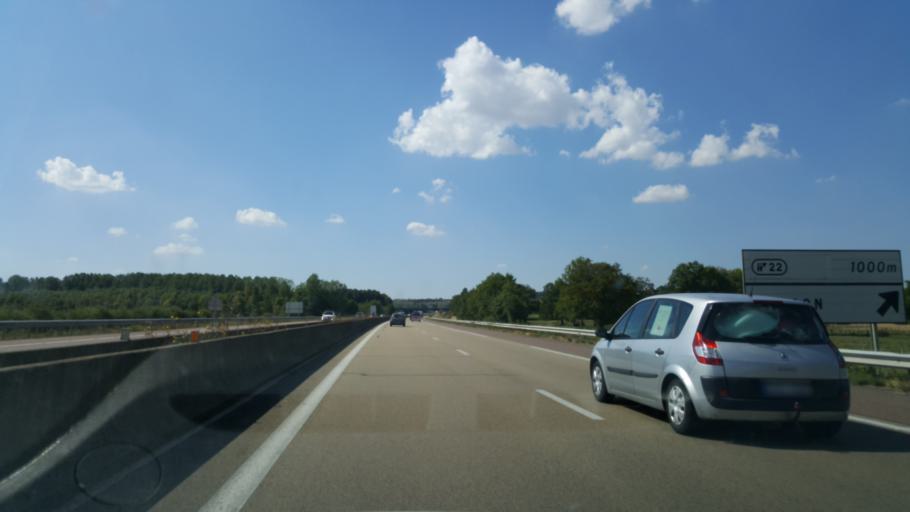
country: FR
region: Bourgogne
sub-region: Departement de l'Yonne
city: Avallon
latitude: 47.5074
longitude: 4.0074
